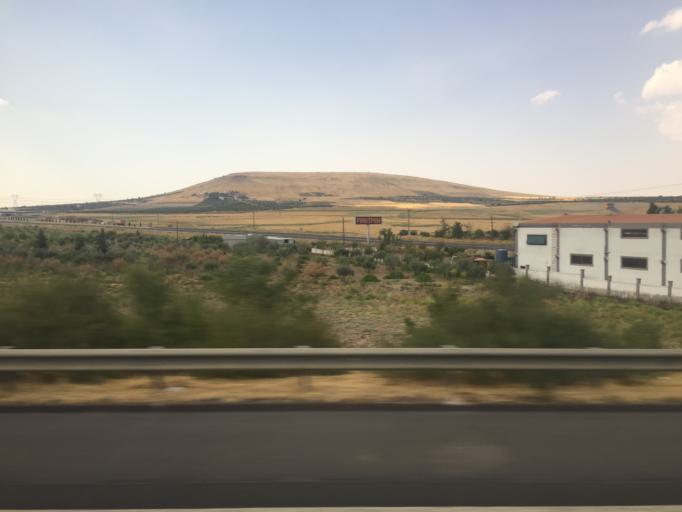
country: TR
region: Sanliurfa
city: Akziyaret
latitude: 37.2646
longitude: 38.7684
